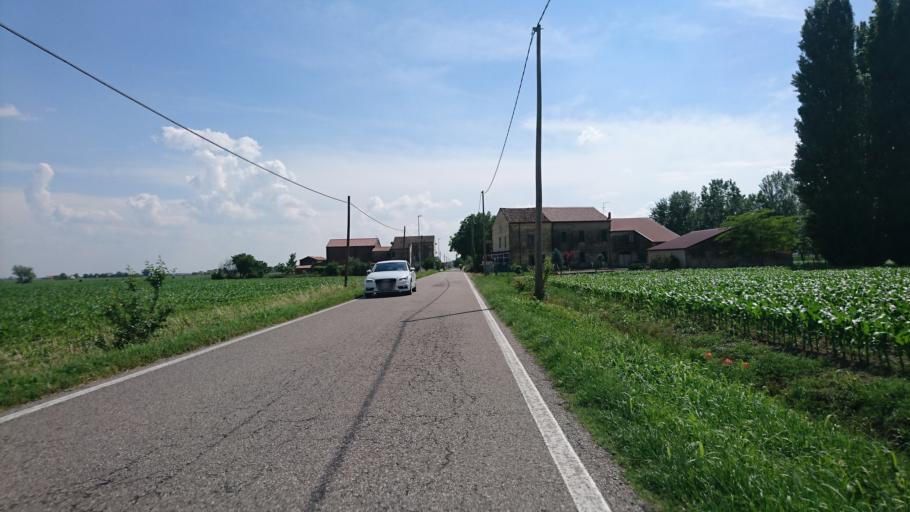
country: IT
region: Veneto
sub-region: Provincia di Rovigo
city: Castelmassa
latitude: 45.0697
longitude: 11.3361
